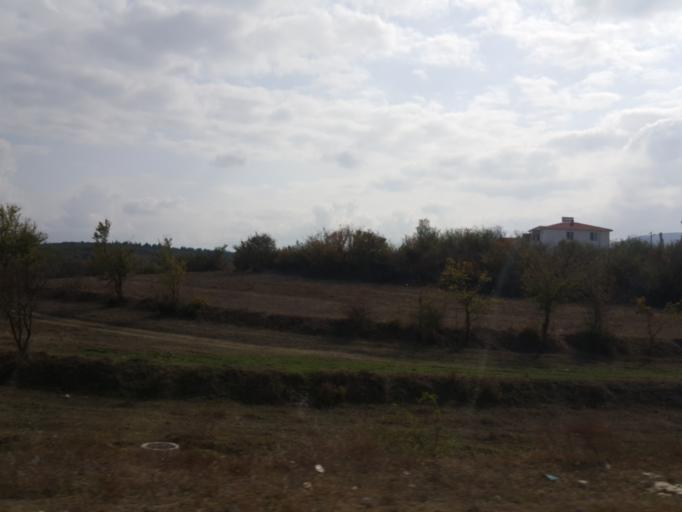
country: TR
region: Sinop
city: Sarayduzu
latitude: 41.3347
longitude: 34.8593
